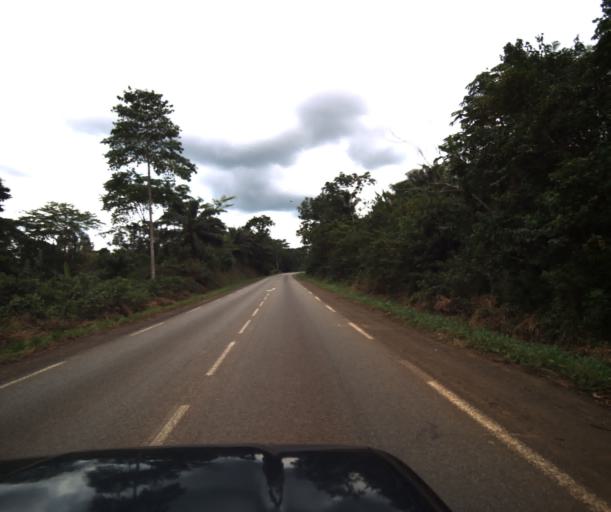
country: CM
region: Littoral
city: Edea
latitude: 3.8385
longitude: 10.4641
